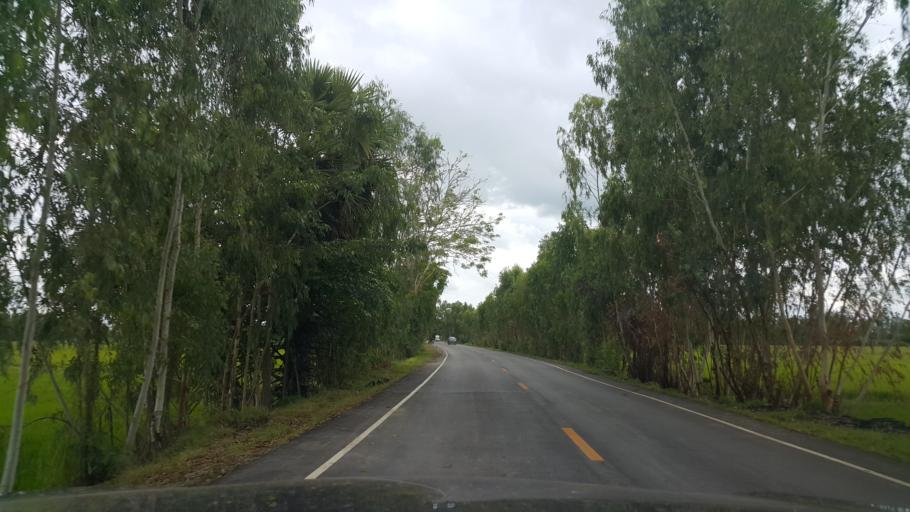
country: TH
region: Sukhothai
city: Kong Krailat
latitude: 16.9161
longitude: 99.8867
